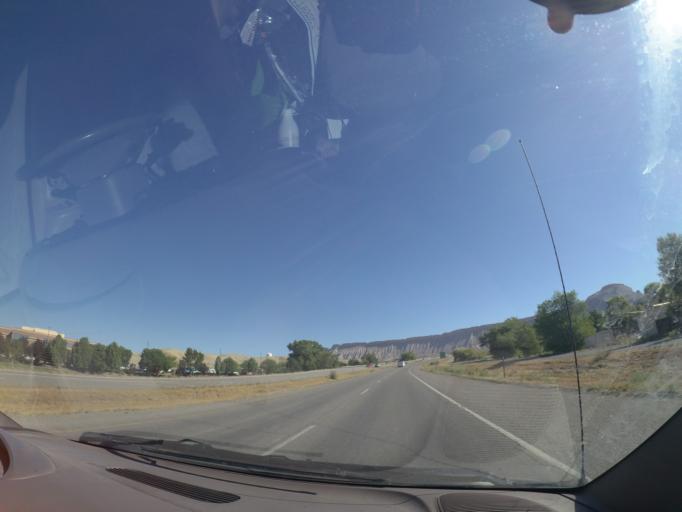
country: US
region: Colorado
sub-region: Mesa County
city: Clifton
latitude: 39.0976
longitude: -108.4487
